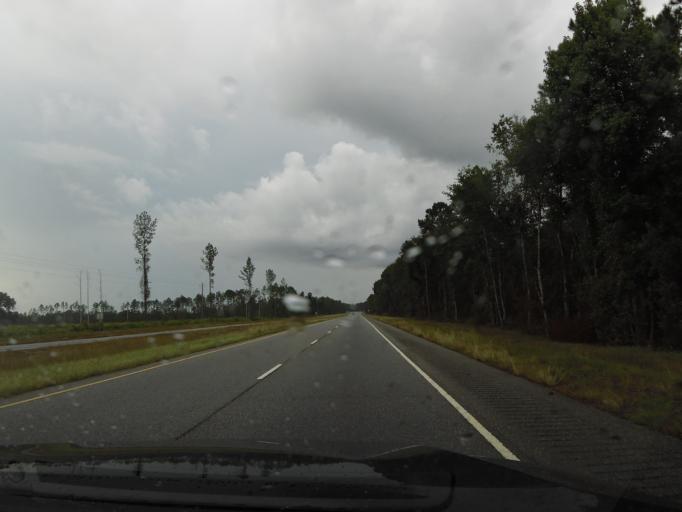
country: US
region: Georgia
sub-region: Wayne County
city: Jesup
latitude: 31.5447
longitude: -81.8058
